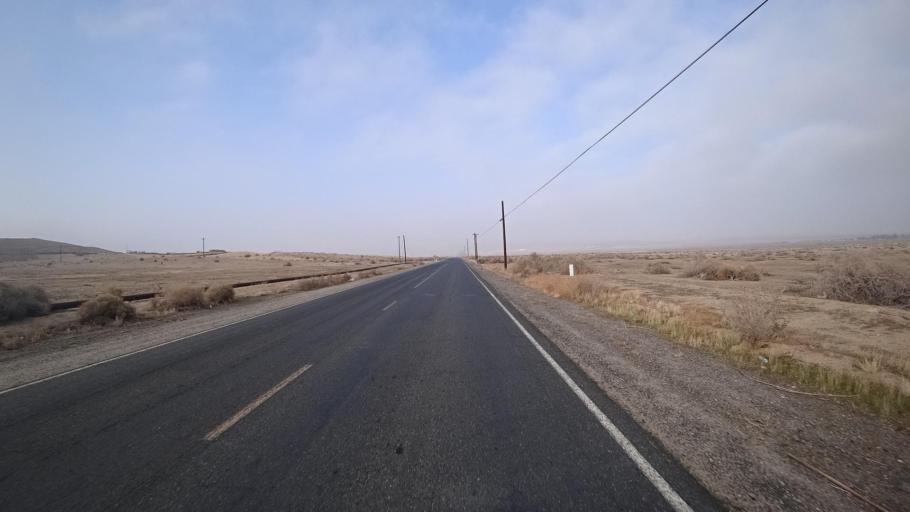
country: US
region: California
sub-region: Kern County
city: Ford City
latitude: 35.2009
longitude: -119.4456
